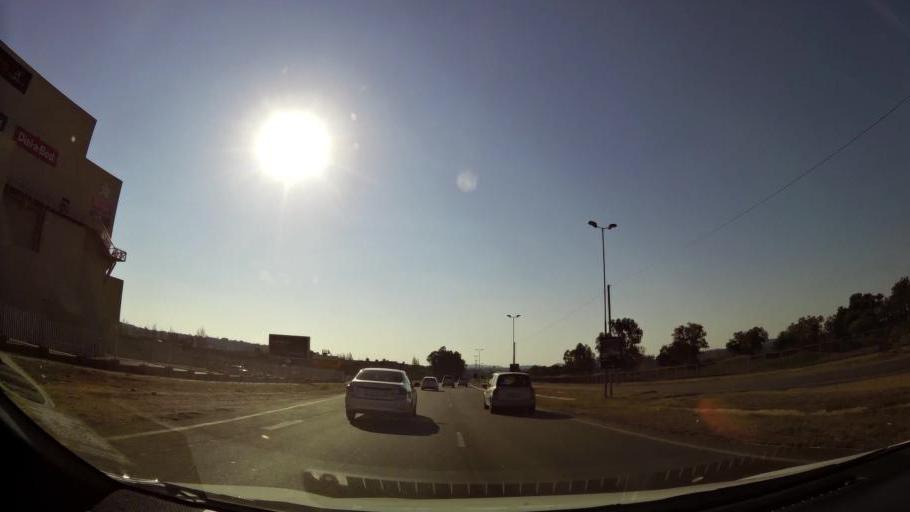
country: ZA
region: Gauteng
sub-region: City of Tshwane Metropolitan Municipality
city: Centurion
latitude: -25.8166
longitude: 28.3044
